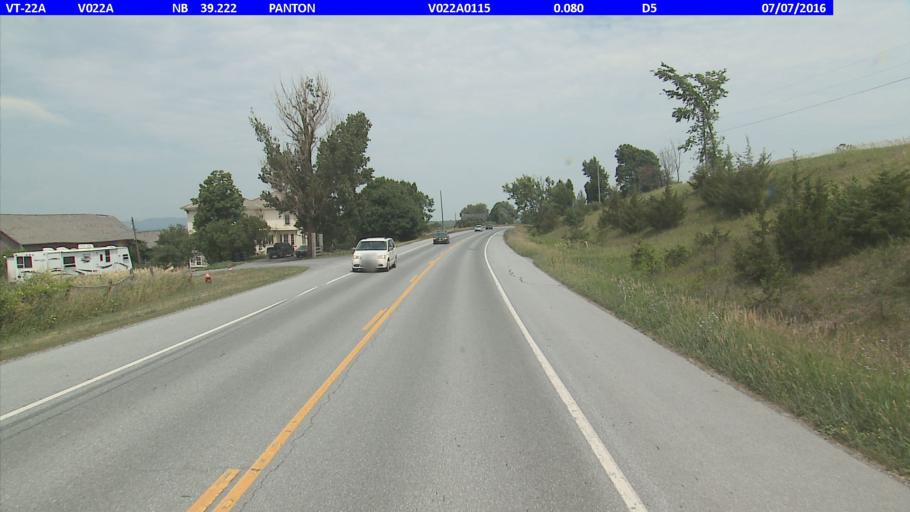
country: US
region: Vermont
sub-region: Addison County
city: Vergennes
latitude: 44.1208
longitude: -73.2935
